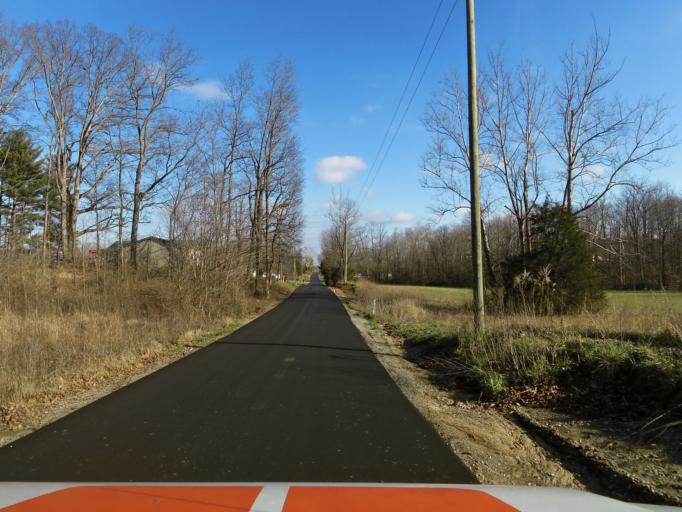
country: US
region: Indiana
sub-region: Jennings County
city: Country Squire Lakes
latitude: 38.9832
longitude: -85.7832
